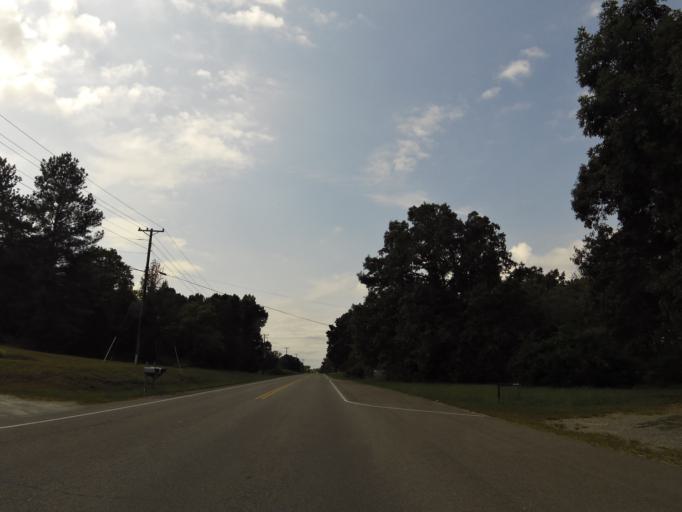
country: US
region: Tennessee
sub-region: Humphreys County
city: Waverly
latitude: 35.8742
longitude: -87.8051
